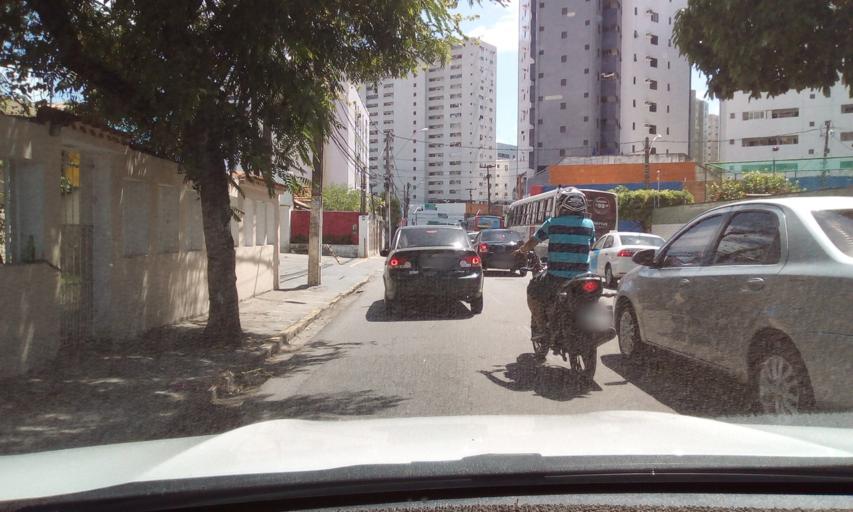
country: BR
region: Pernambuco
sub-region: Recife
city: Recife
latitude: -8.1335
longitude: -34.9041
